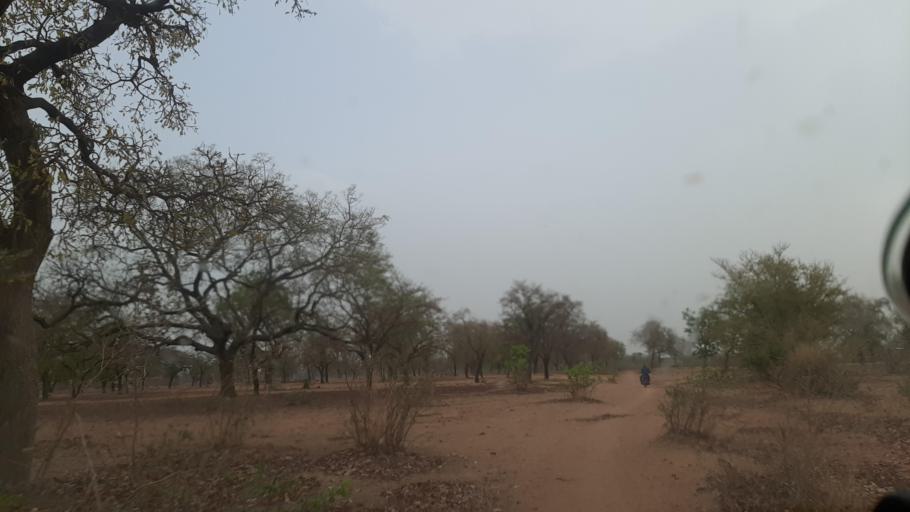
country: BF
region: Boucle du Mouhoun
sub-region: Province des Banwa
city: Salanso
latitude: 11.8674
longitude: -4.4449
